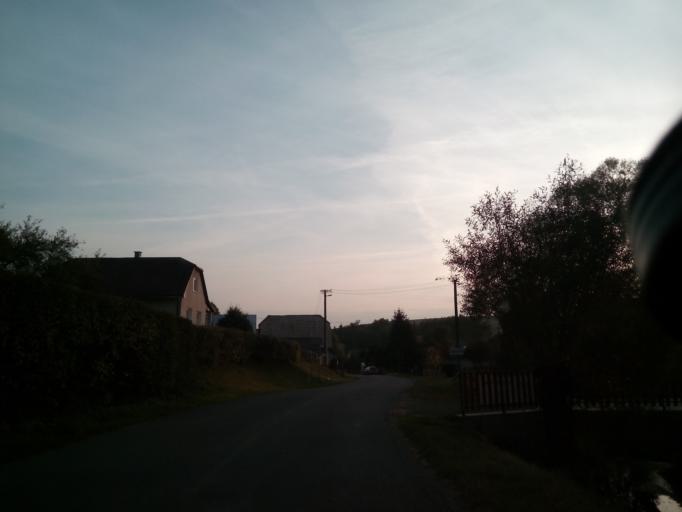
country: SK
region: Presovsky
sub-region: Okres Bardejov
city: Bardejov
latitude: 49.3386
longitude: 21.3354
